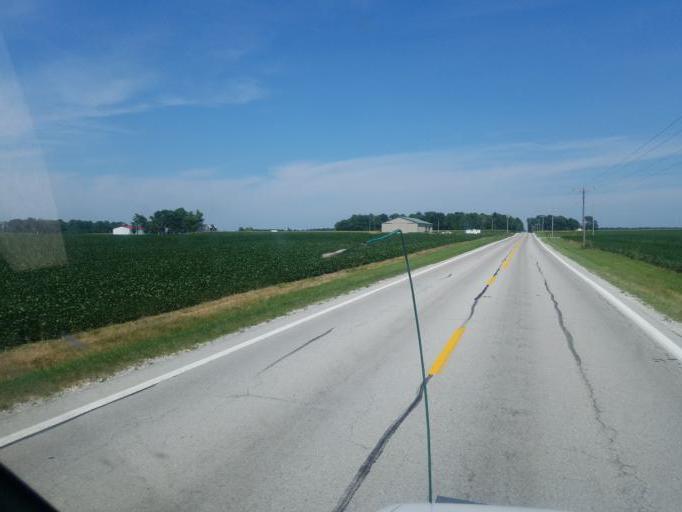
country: US
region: Ohio
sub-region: Shelby County
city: Botkins
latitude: 40.4967
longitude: -84.2283
